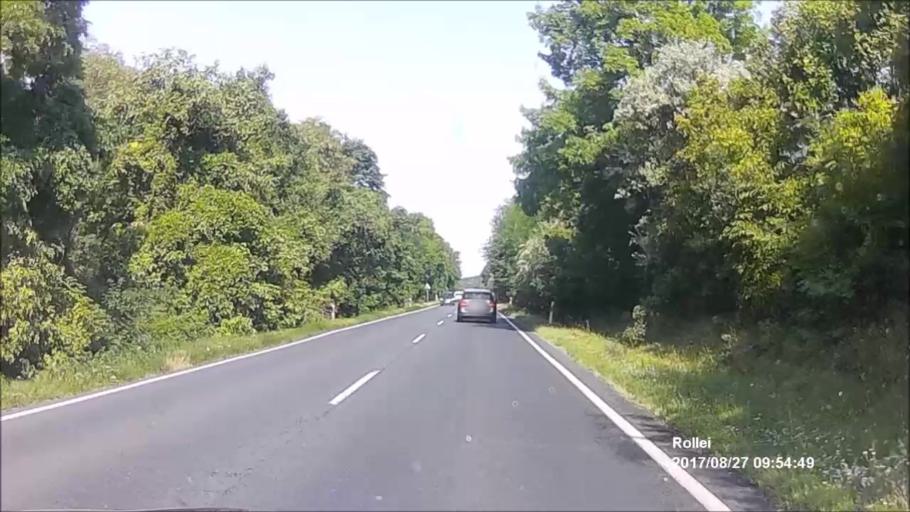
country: AT
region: Burgenland
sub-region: Eisenstadt-Umgebung
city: Klingenbach
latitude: 47.7257
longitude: 16.5603
